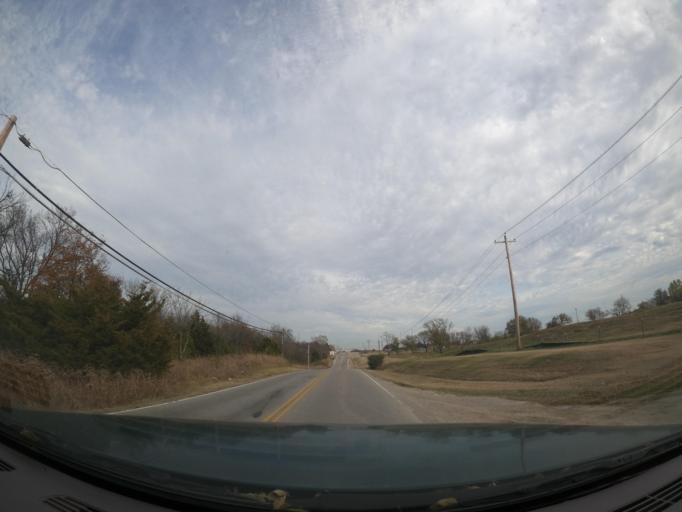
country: US
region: Oklahoma
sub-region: Tulsa County
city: Turley
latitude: 36.2061
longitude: -95.9622
